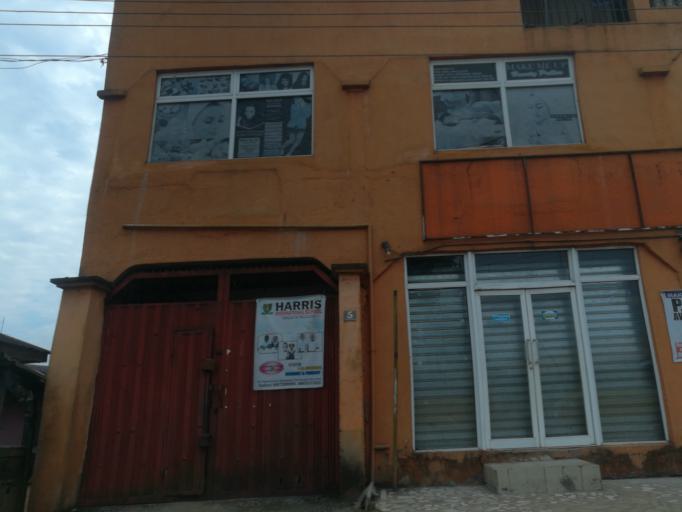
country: NG
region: Rivers
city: Port Harcourt
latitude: 4.8156
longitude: 6.9548
